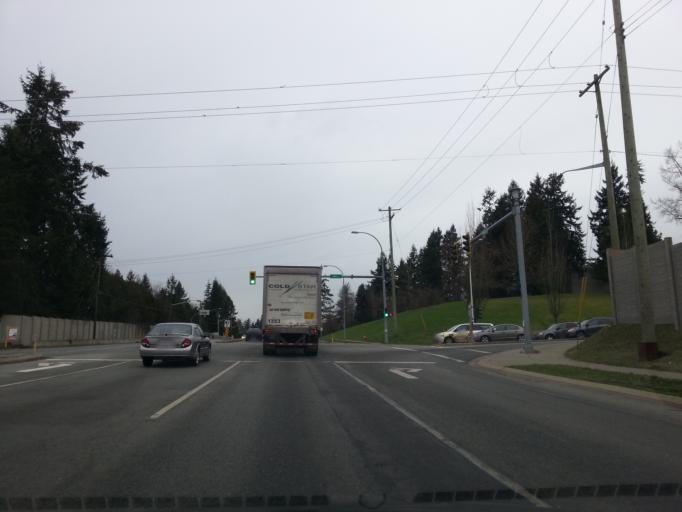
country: CA
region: British Columbia
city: Surrey
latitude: 49.1046
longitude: -122.8230
